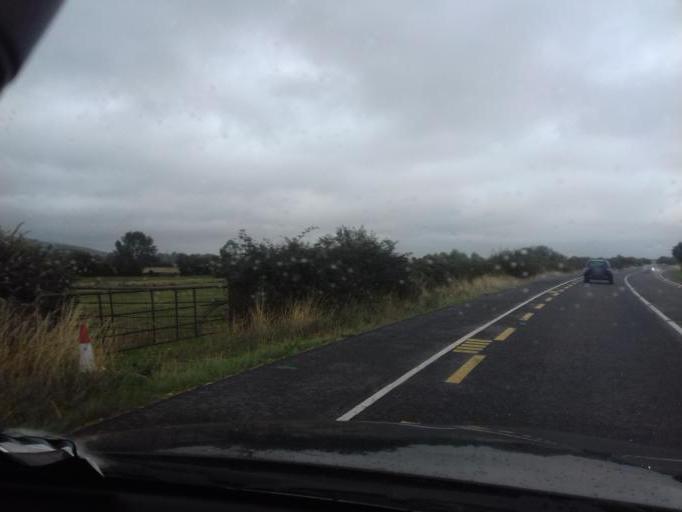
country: IE
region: Leinster
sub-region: County Carlow
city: Bagenalstown
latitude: 52.7481
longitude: -6.9667
